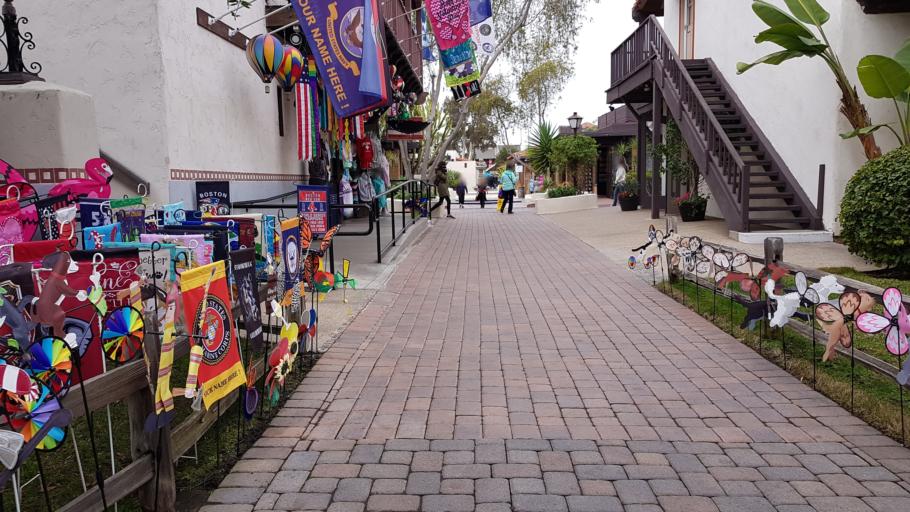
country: US
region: California
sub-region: San Diego County
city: San Diego
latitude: 32.7090
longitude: -117.1705
